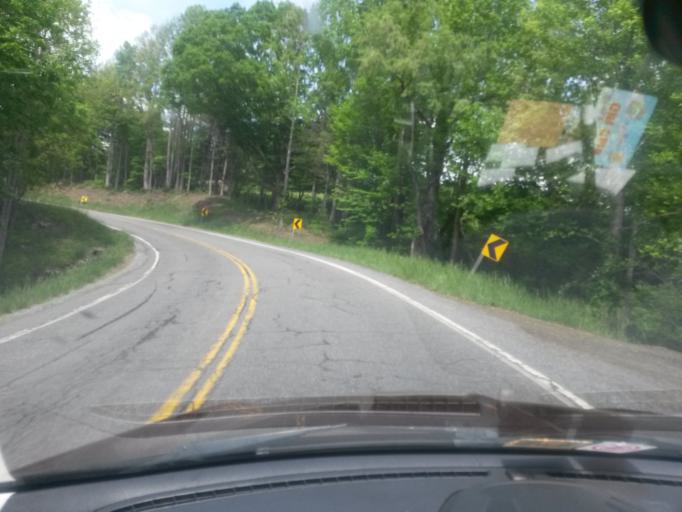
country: US
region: Virginia
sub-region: Floyd County
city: Floyd
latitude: 36.8986
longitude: -80.3189
